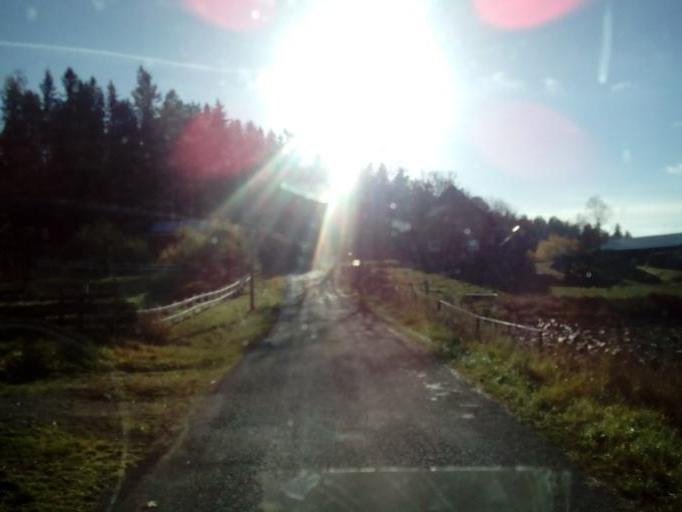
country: SE
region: Kalmar
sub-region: Vasterviks Kommun
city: Ankarsrum
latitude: 57.8068
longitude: 16.1664
